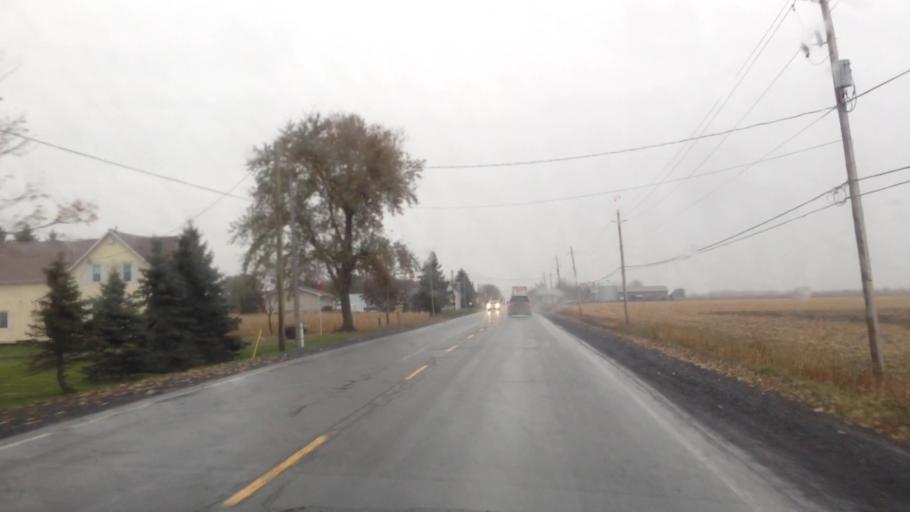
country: CA
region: Ontario
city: Bourget
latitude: 45.3246
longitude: -75.3424
